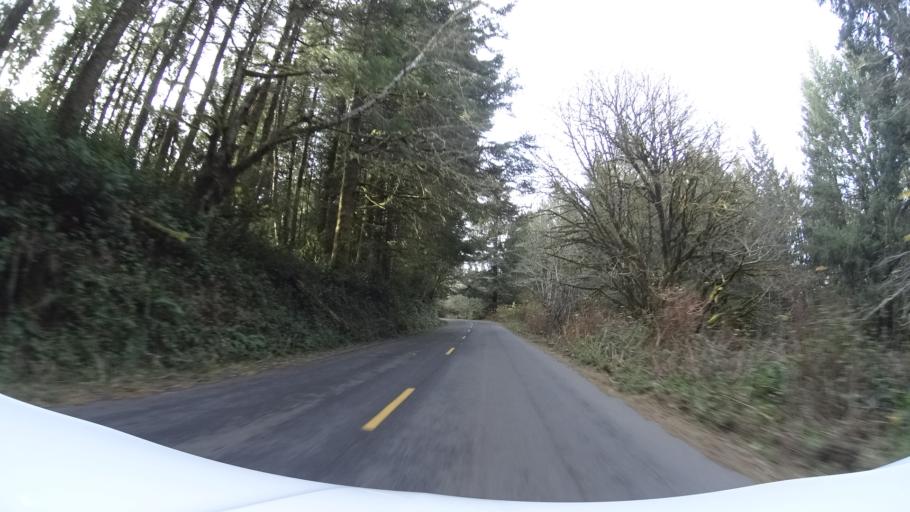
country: US
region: California
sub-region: Humboldt County
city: Ferndale
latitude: 40.5350
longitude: -124.2716
